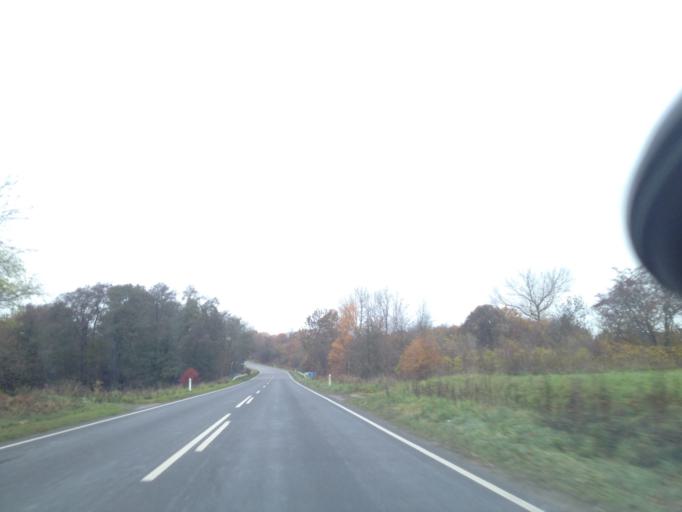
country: DK
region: South Denmark
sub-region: Nordfyns Kommune
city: Sonderso
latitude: 55.4305
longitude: 10.2471
